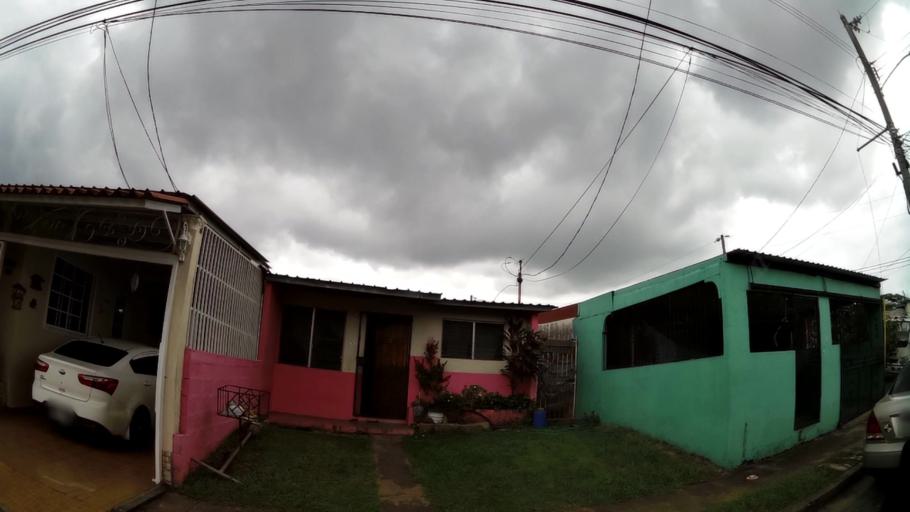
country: PA
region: Panama
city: Tocumen
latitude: 9.0563
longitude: -79.4141
